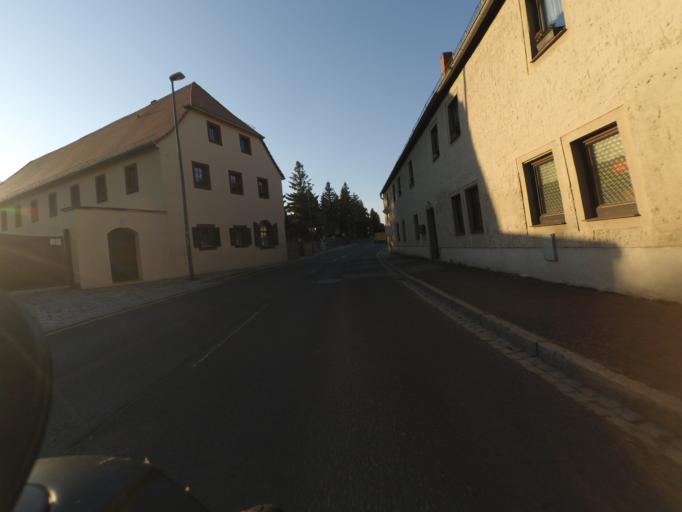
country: DE
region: Saxony
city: Kreischa
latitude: 50.9872
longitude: 13.8028
